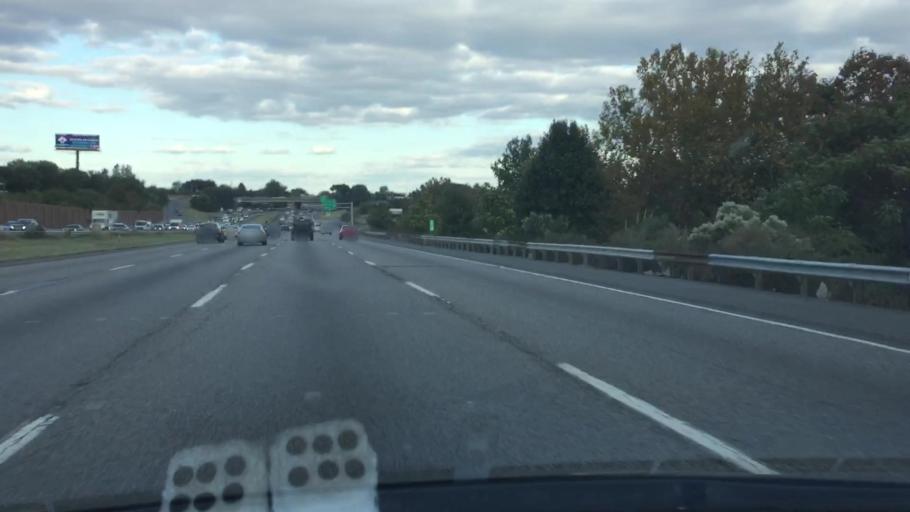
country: US
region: Pennsylvania
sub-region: Delaware County
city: Woodlyn
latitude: 39.8681
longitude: -75.3300
